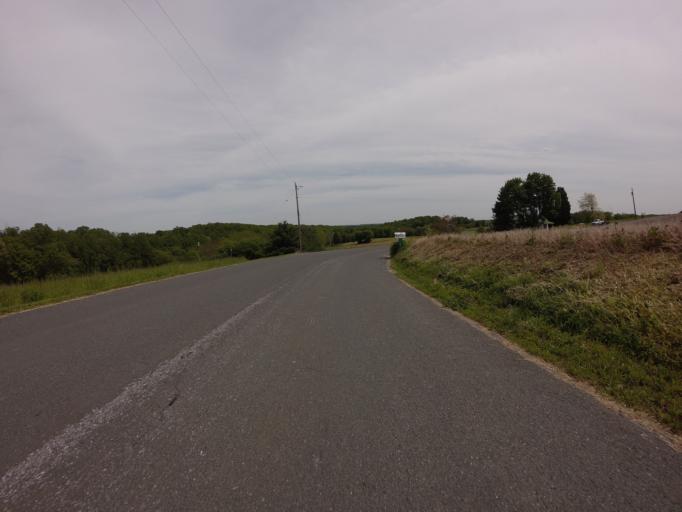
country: US
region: Maryland
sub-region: Carroll County
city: Eldersburg
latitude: 39.4870
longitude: -76.9746
